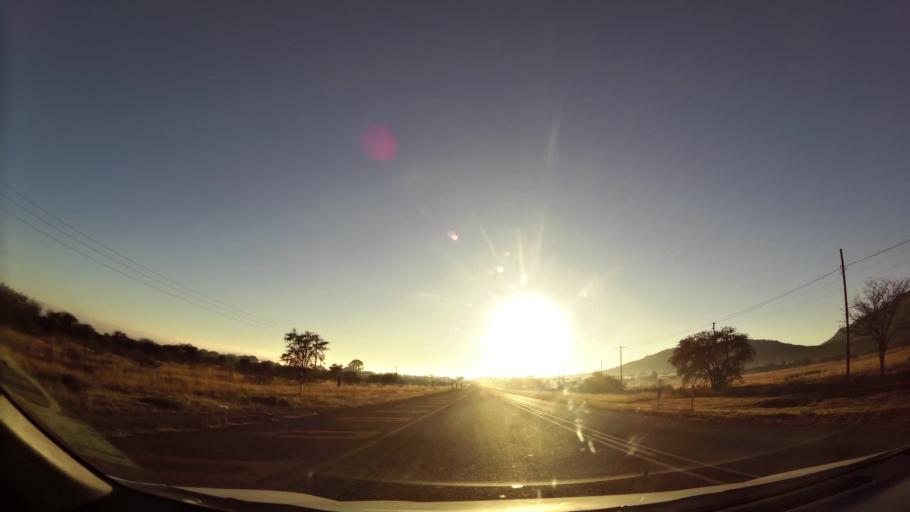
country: ZA
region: Limpopo
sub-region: Capricorn District Municipality
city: Polokwane
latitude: -24.0113
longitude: 29.3250
